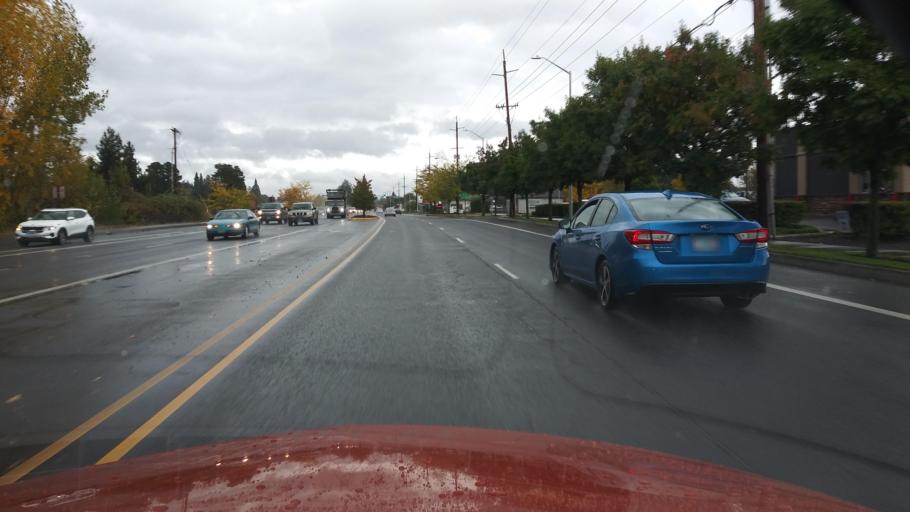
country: US
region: Oregon
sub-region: Washington County
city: Cornelius
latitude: 45.5200
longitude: -123.0433
